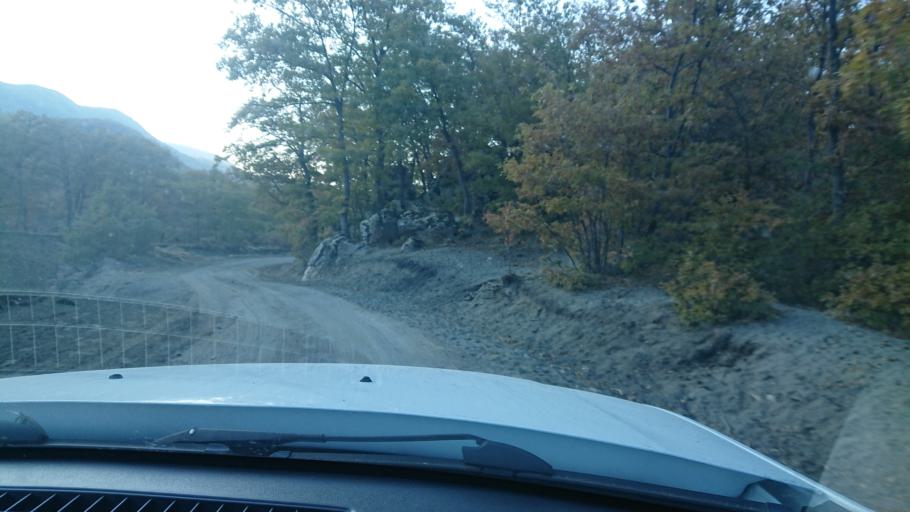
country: TR
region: Aksaray
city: Taspinar
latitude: 38.1653
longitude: 34.2076
